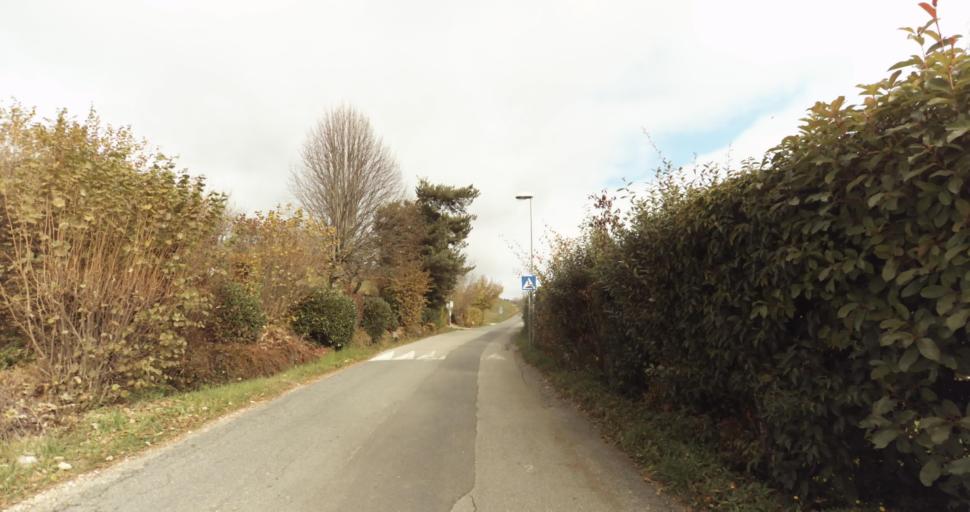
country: FR
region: Rhone-Alpes
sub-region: Departement de la Haute-Savoie
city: Epagny
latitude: 45.9658
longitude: 6.0830
